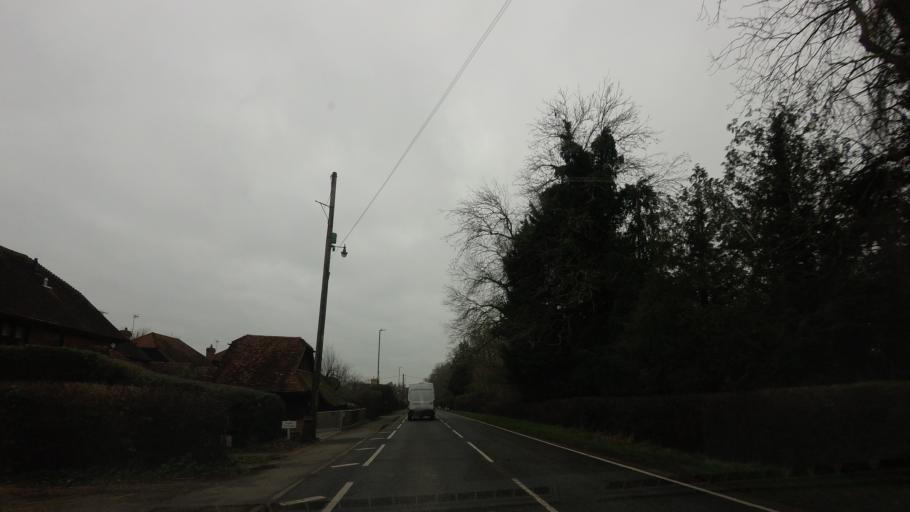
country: GB
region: England
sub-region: Kent
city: Staplehurst
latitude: 51.1514
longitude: 0.5521
